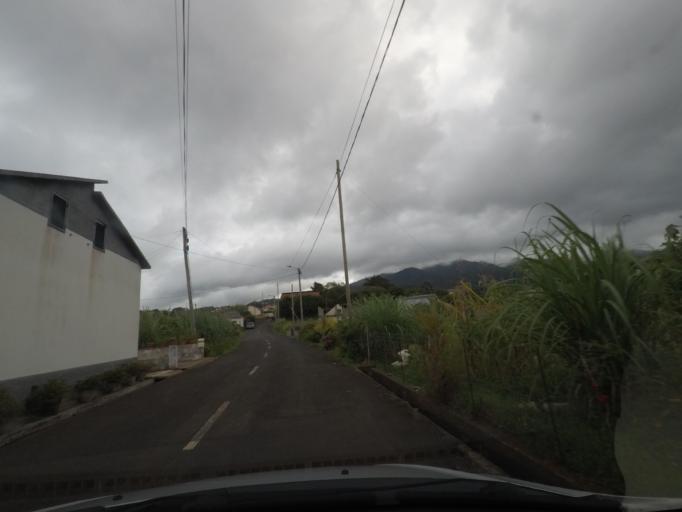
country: PT
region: Madeira
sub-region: Santana
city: Santana
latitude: 32.8143
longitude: -16.8790
